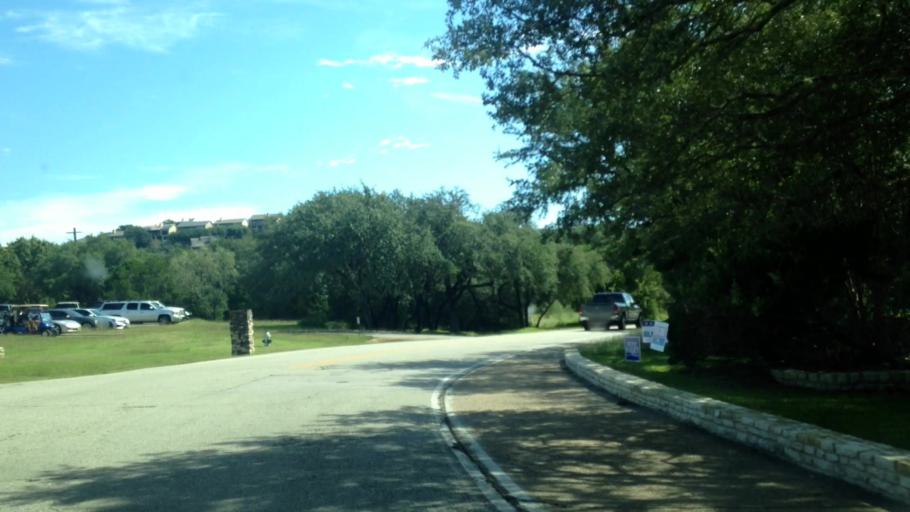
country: US
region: Texas
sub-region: Travis County
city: Lakeway
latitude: 30.3589
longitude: -97.9676
